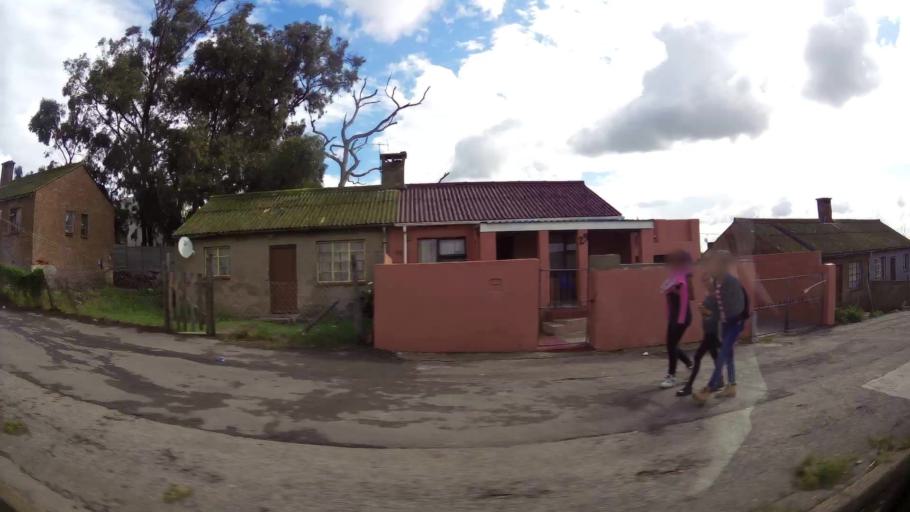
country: ZA
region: Eastern Cape
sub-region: Nelson Mandela Bay Metropolitan Municipality
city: Port Elizabeth
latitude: -33.9313
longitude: 25.5672
